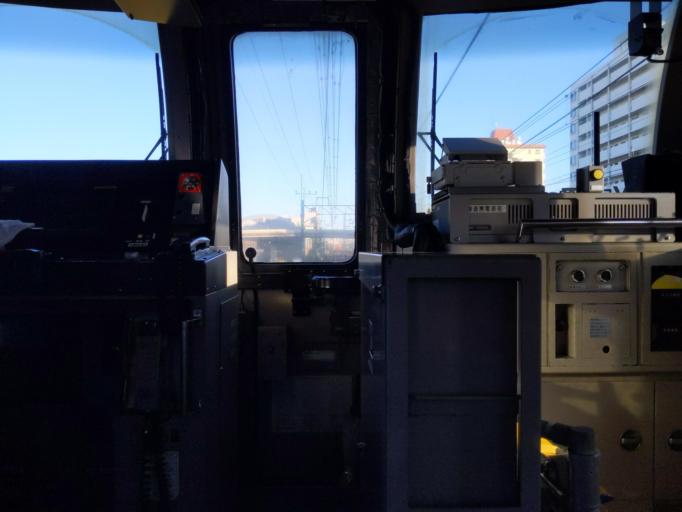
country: JP
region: Chiba
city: Funabashi
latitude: 35.7047
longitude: 139.9656
